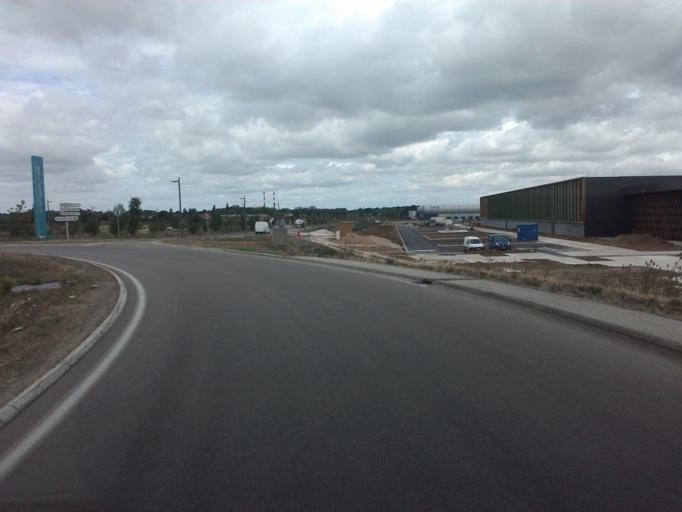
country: FR
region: Franche-Comte
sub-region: Departement du Jura
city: Choisey
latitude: 47.0531
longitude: 5.4362
